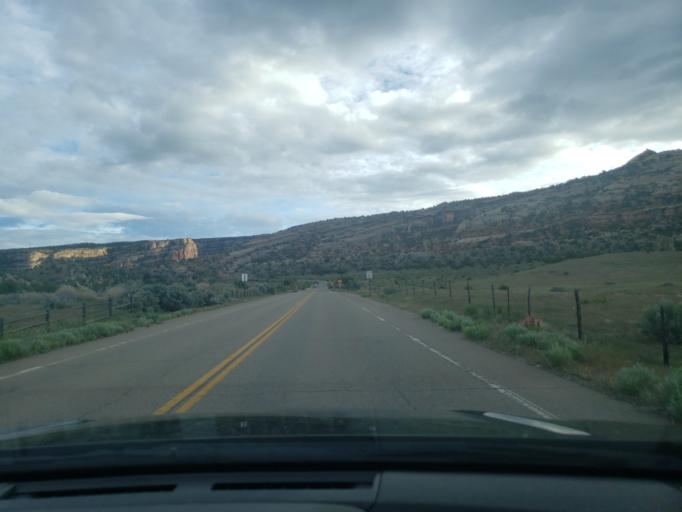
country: US
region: Colorado
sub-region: Mesa County
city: Redlands
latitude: 39.0370
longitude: -108.6297
